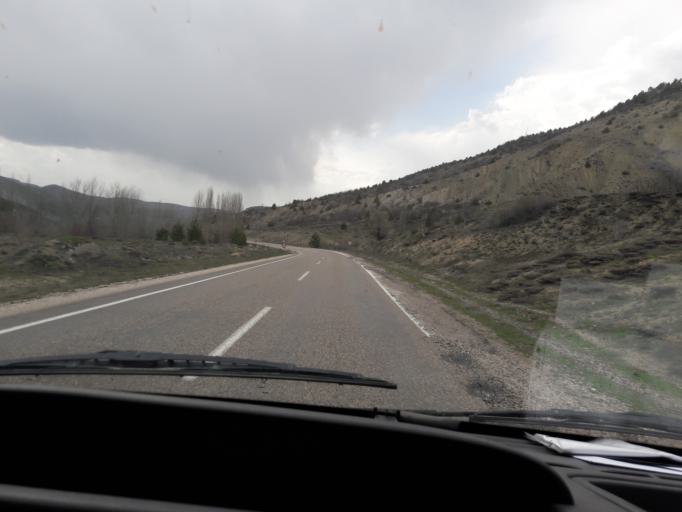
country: TR
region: Giresun
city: Alucra
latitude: 40.2737
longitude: 38.8577
